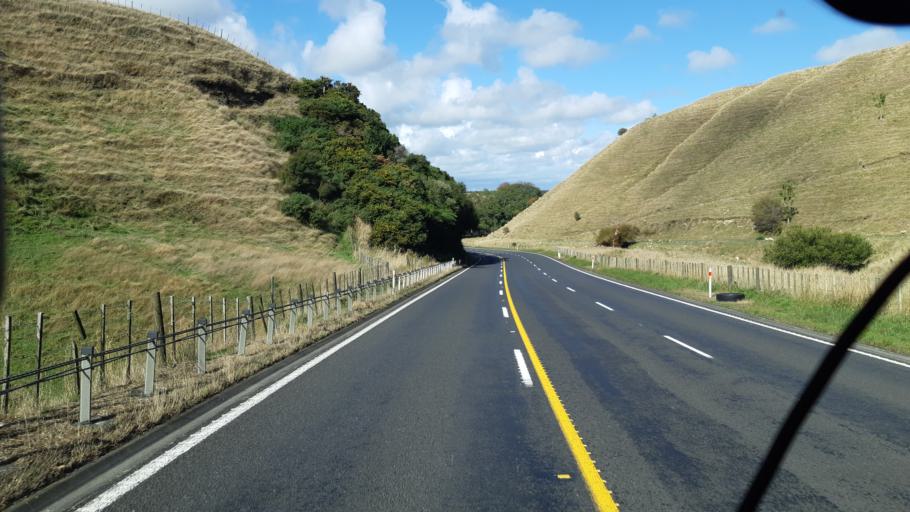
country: NZ
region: Manawatu-Wanganui
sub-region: Wanganui District
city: Wanganui
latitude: -40.0303
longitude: 175.2035
